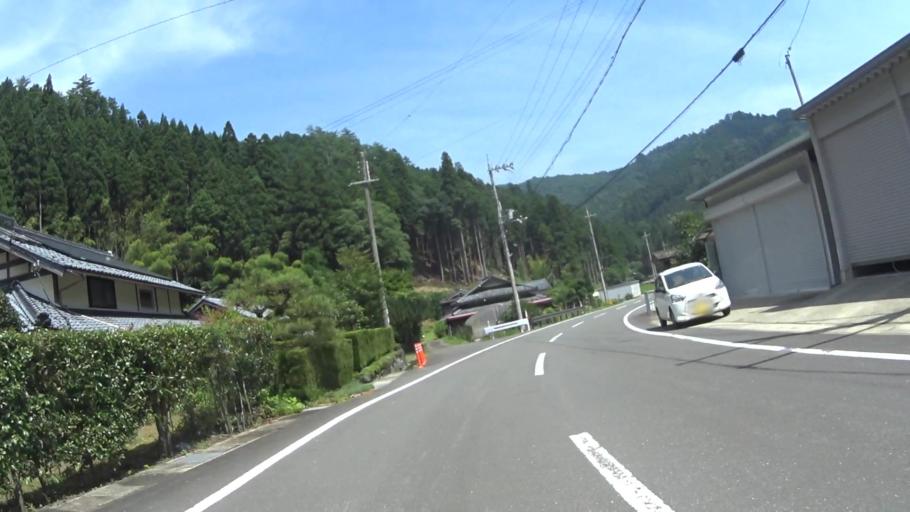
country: JP
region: Kyoto
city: Maizuru
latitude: 35.3421
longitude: 135.5299
